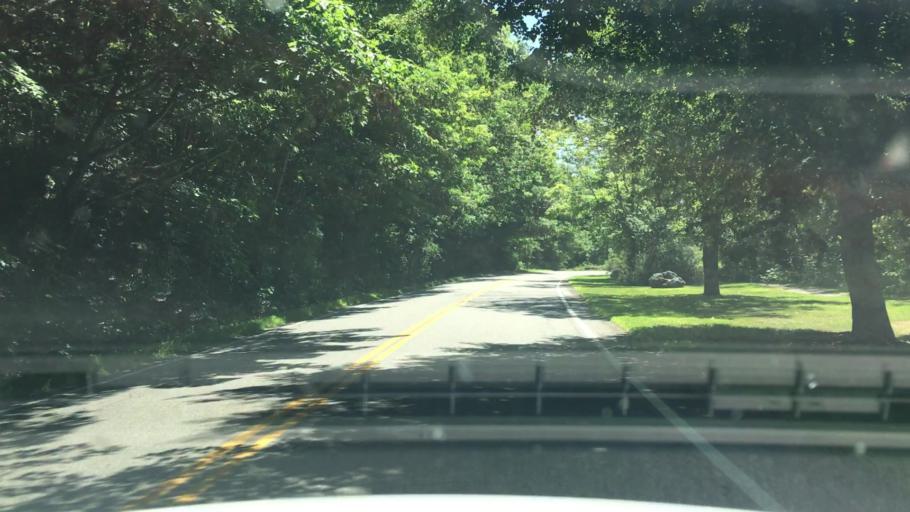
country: US
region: Maine
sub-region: Penobscot County
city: Bangor
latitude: 44.8142
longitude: -68.7854
